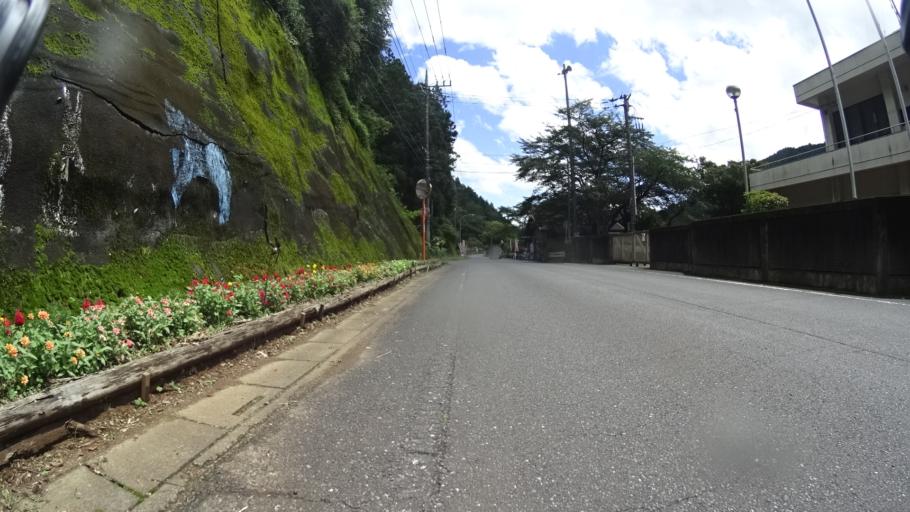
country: JP
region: Tokyo
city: Ome
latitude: 35.8750
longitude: 139.1755
